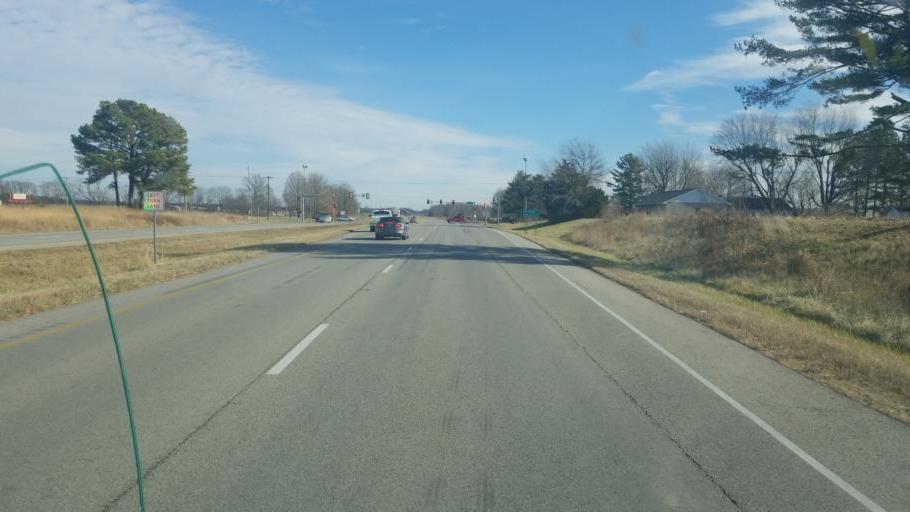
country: US
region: Illinois
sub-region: Williamson County
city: Marion
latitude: 37.7291
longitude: -88.8573
